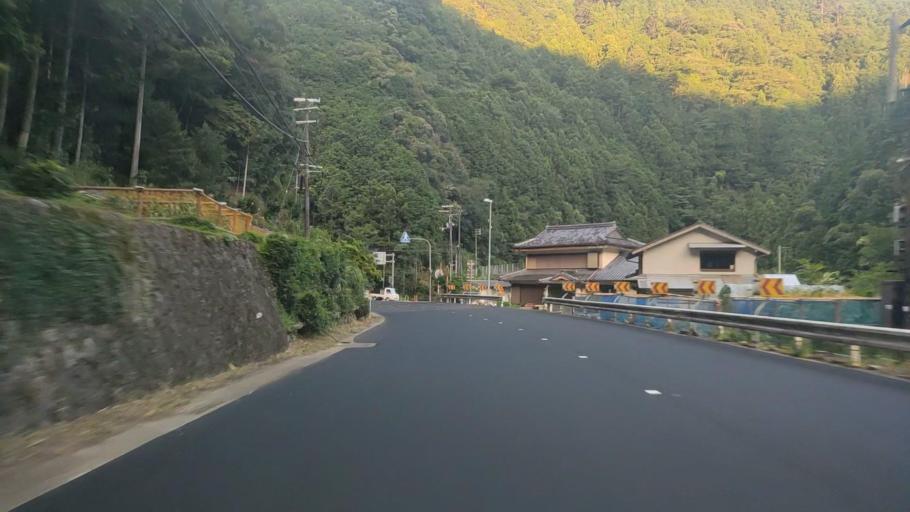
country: JP
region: Wakayama
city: Shingu
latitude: 33.8067
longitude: 135.7124
